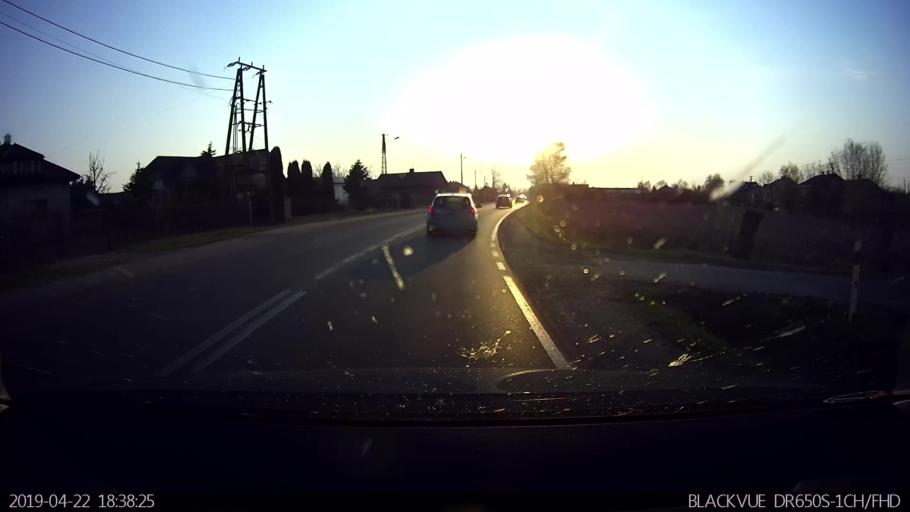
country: PL
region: Masovian Voivodeship
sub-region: Powiat wolominski
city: Dabrowka
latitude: 52.4410
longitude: 21.2970
